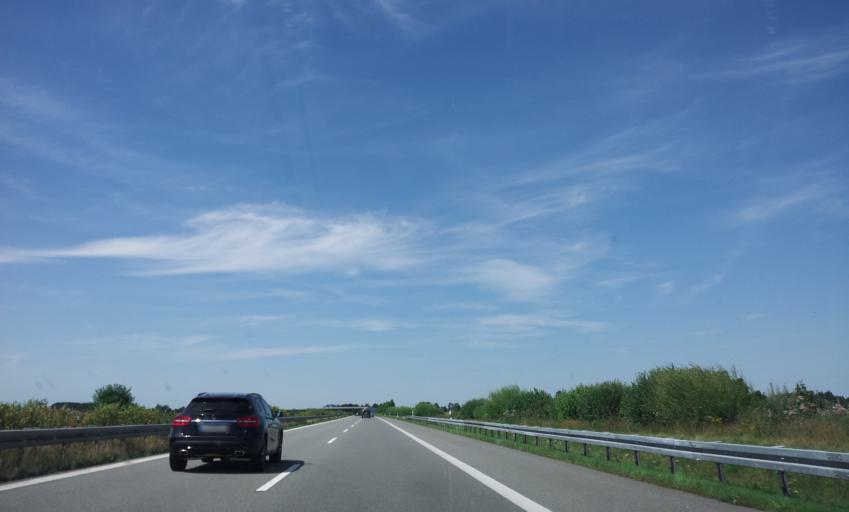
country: DE
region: Mecklenburg-Vorpommern
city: Dersekow
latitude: 54.0634
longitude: 13.2308
